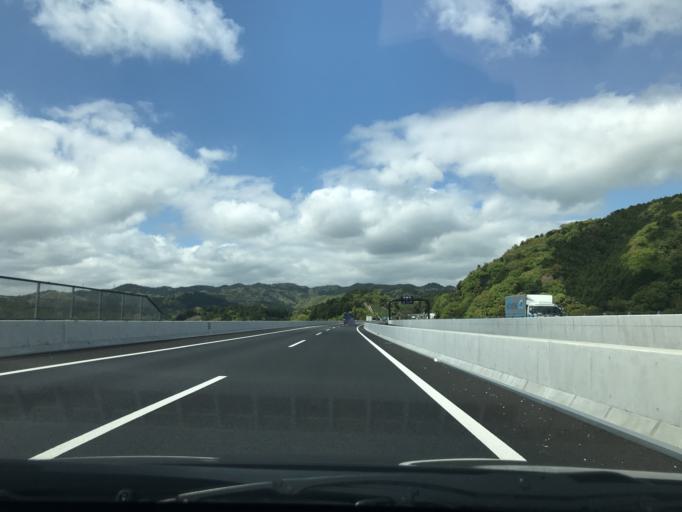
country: JP
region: Osaka
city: Takatsuki
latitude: 34.8885
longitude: 135.6129
